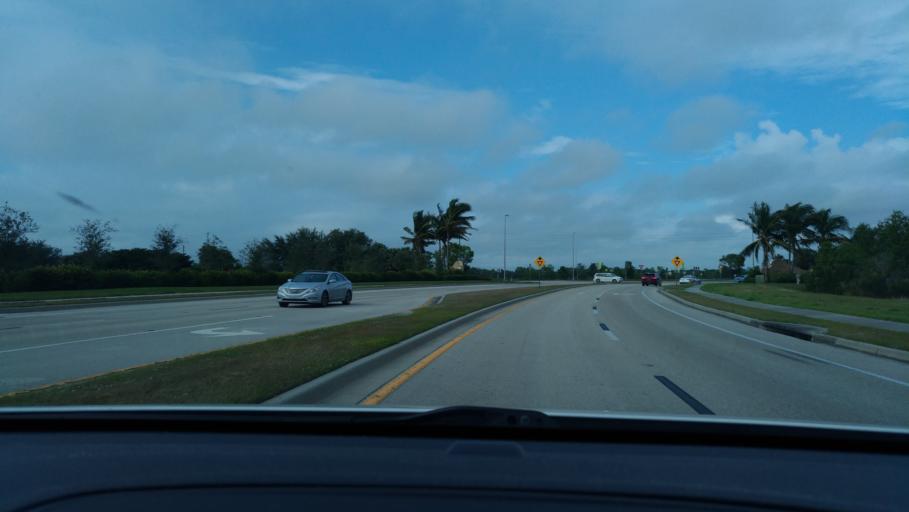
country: US
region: Florida
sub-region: Lee County
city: Estero
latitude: 26.4189
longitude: -81.8065
